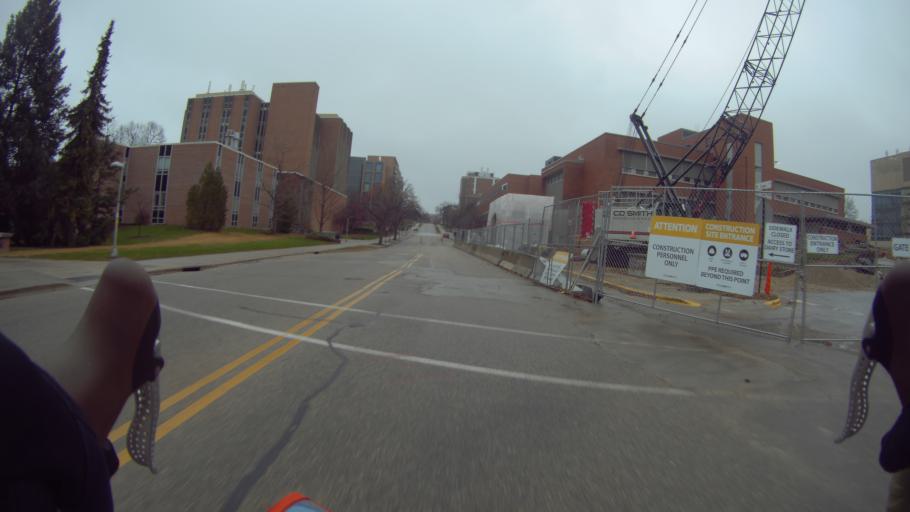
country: US
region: Wisconsin
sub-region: Dane County
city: Madison
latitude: 43.0752
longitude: -89.4148
